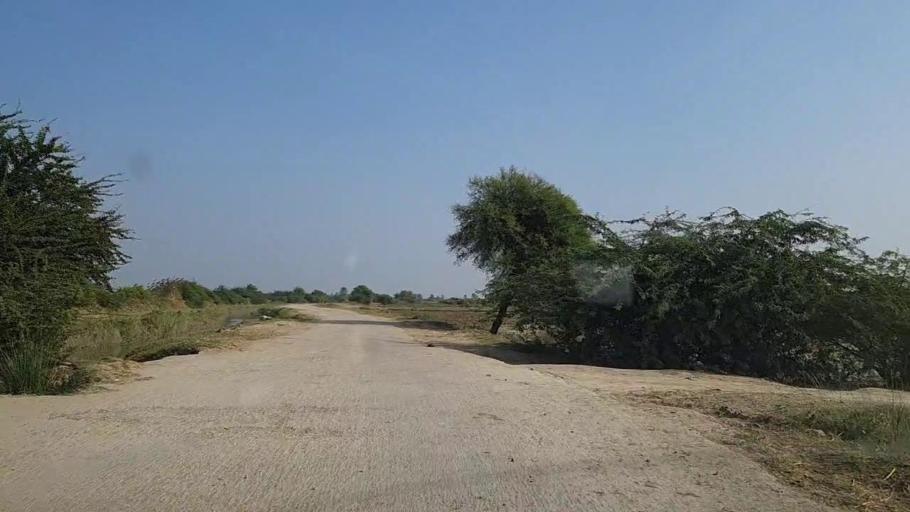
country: PK
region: Sindh
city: Mirpur Sakro
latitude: 24.5962
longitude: 67.5962
